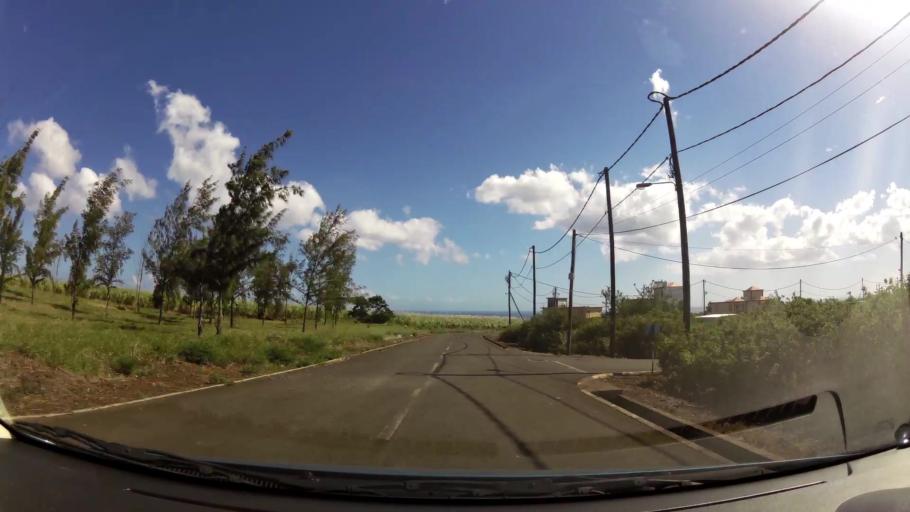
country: MU
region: Black River
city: Cascavelle
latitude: -20.2701
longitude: 57.4154
